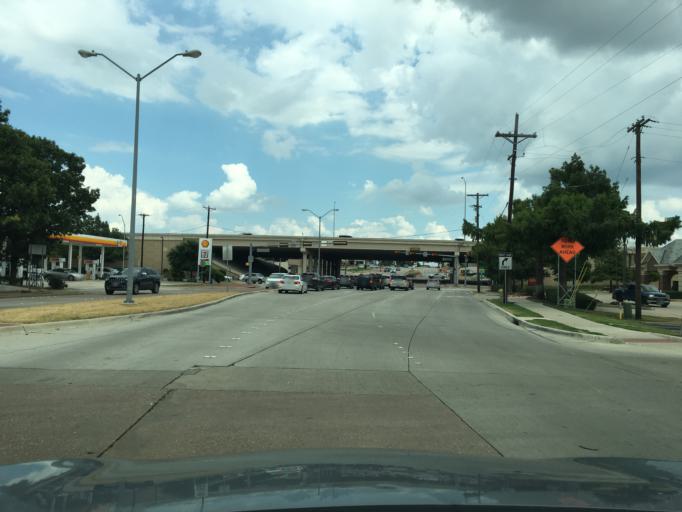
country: US
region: Texas
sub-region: Collin County
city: Plano
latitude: 33.0195
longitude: -96.7114
